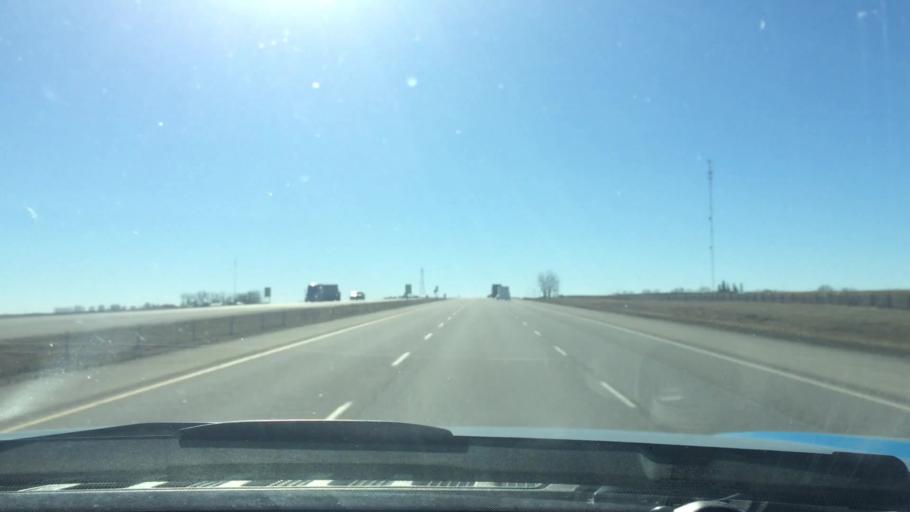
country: CA
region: Alberta
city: Crossfield
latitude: 51.4252
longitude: -114.0021
